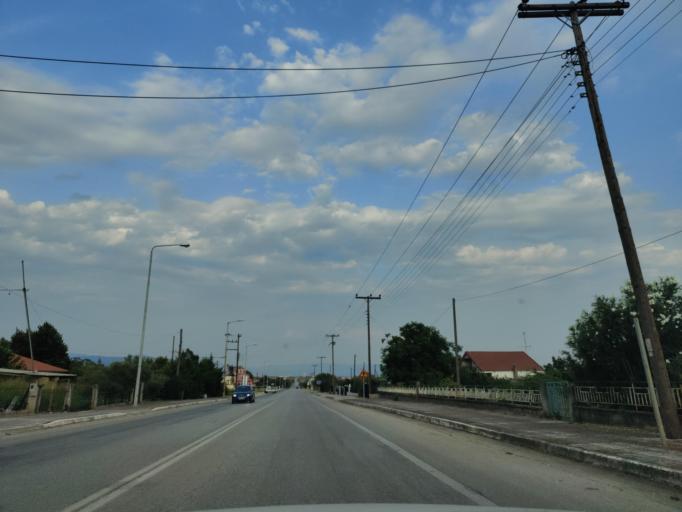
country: GR
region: East Macedonia and Thrace
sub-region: Nomos Dramas
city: Petroussa
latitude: 41.1694
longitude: 24.0419
